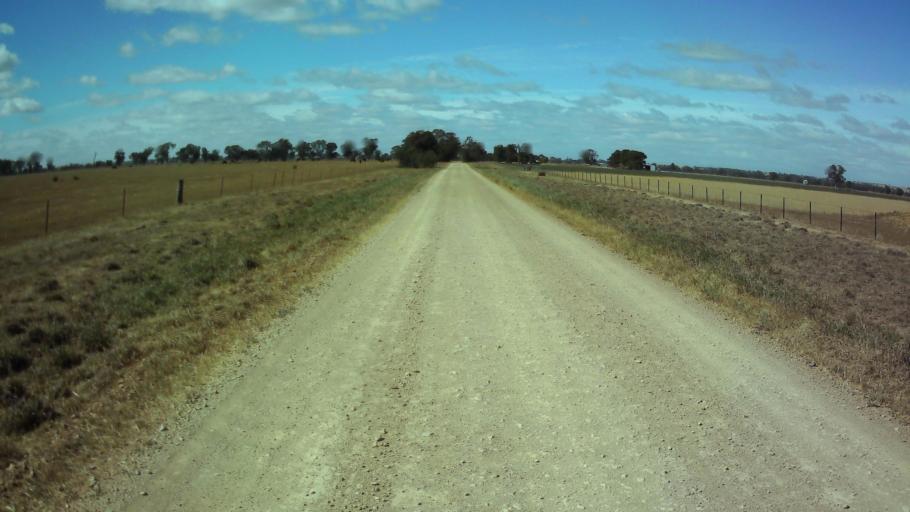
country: AU
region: New South Wales
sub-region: Weddin
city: Grenfell
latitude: -34.0229
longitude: 148.3188
